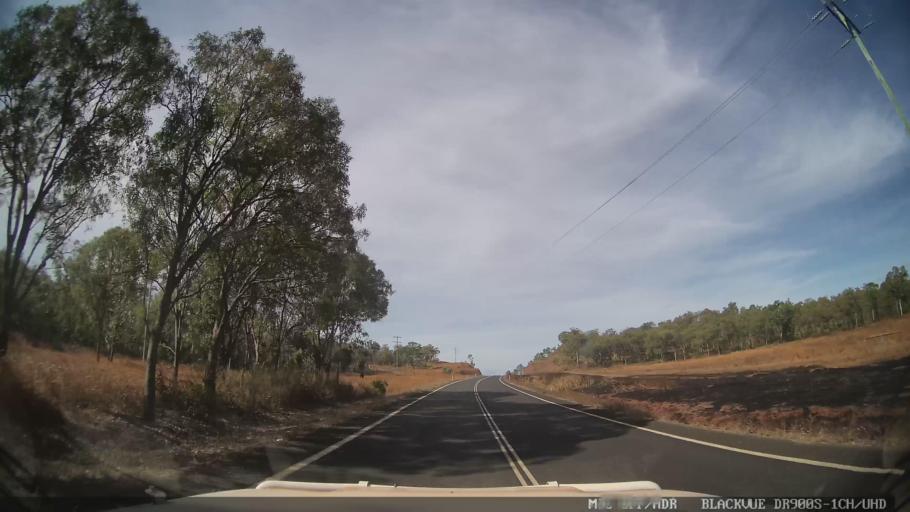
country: AU
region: Queensland
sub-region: Cook
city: Cooktown
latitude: -15.5978
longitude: 145.2275
